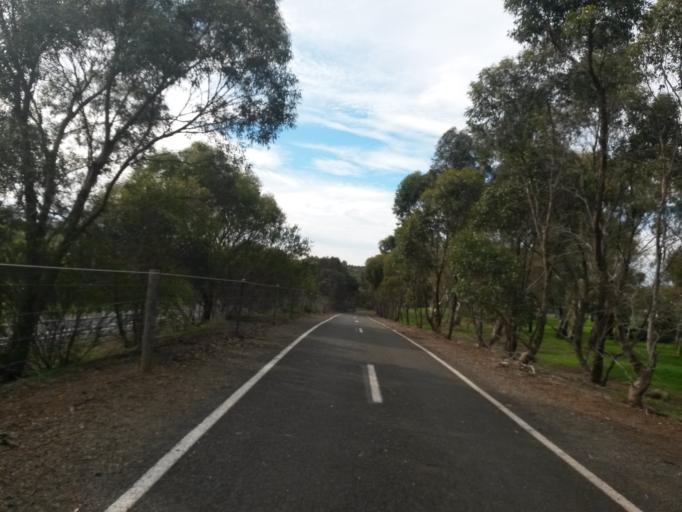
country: AU
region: South Australia
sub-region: Onkaparinga
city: Reynella
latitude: -35.0895
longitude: 138.5307
